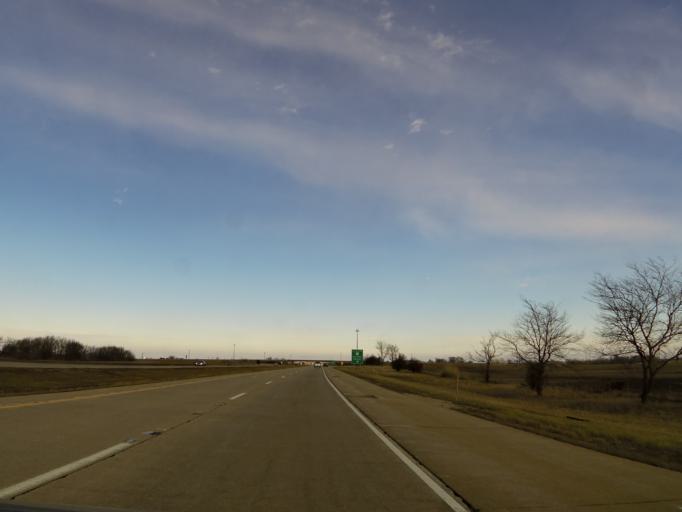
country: US
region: Illinois
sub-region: LaSalle County
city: Oglesby
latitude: 41.2582
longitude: -89.0807
